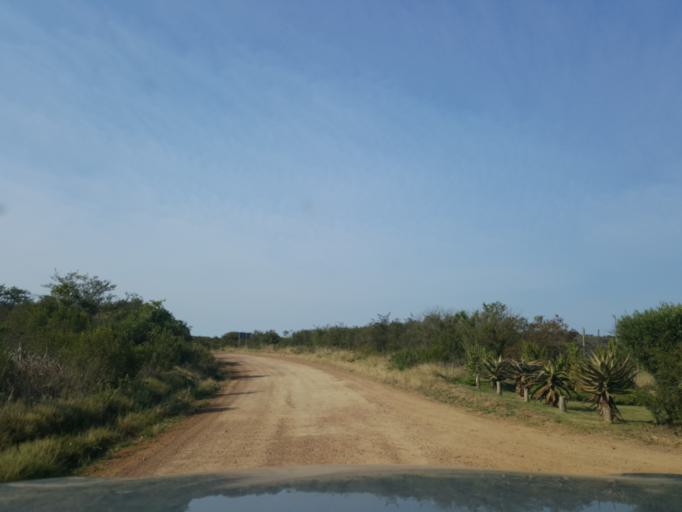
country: ZA
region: Eastern Cape
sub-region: Cacadu District Municipality
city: Grahamstown
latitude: -33.4089
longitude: 26.2997
